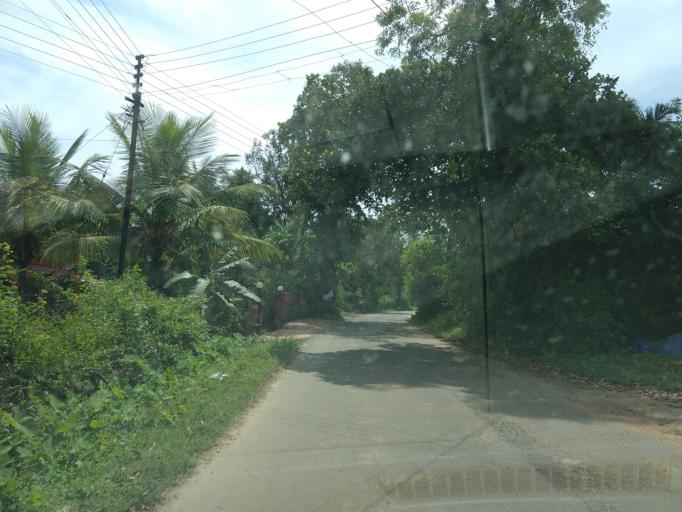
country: IN
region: Maharashtra
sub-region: Sindhudurg
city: Savantvadi
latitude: 15.9598
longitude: 73.7723
